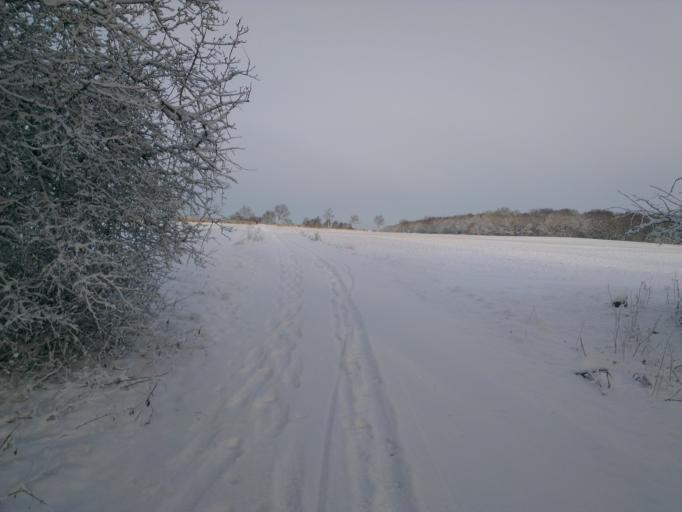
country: DK
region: Capital Region
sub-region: Frederikssund Kommune
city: Jaegerspris
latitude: 55.8516
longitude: 11.9652
